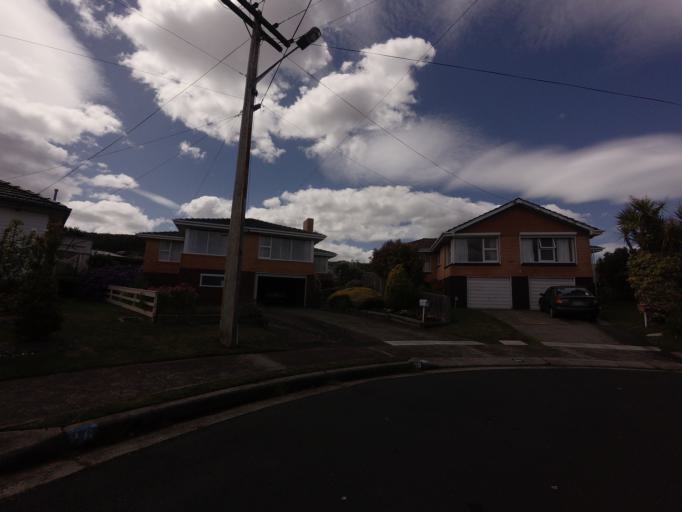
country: AU
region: Tasmania
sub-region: Clarence
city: Howrah
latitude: -42.8778
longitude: 147.4016
